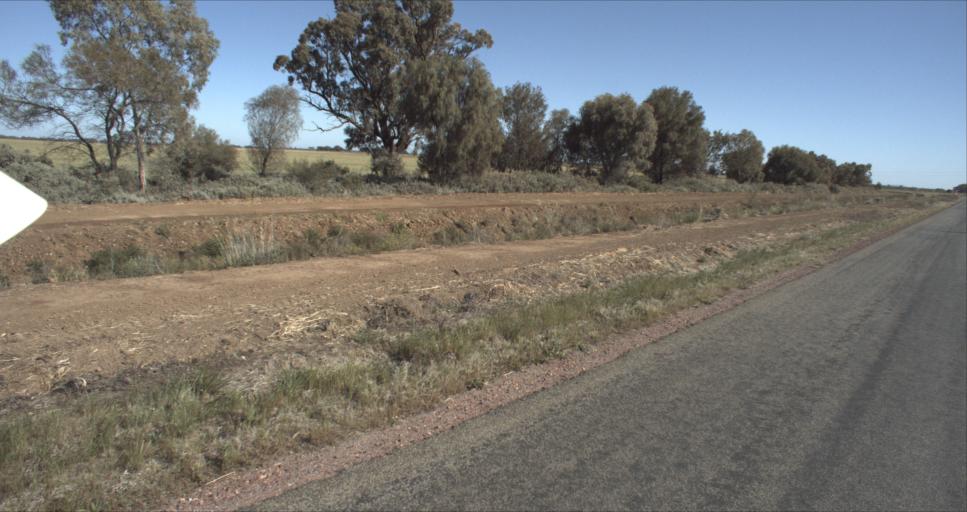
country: AU
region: New South Wales
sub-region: Leeton
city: Leeton
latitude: -34.5529
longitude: 146.2670
